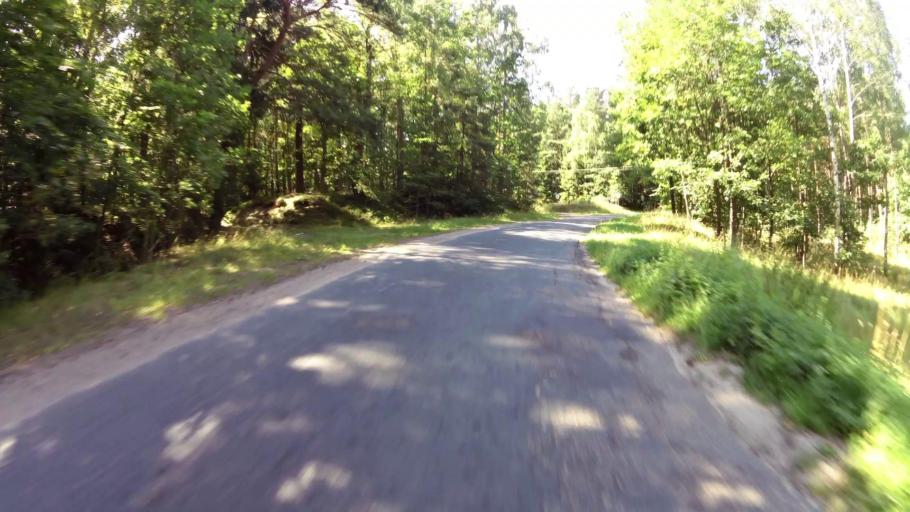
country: PL
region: West Pomeranian Voivodeship
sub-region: Powiat drawski
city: Czaplinek
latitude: 53.4312
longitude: 16.2670
